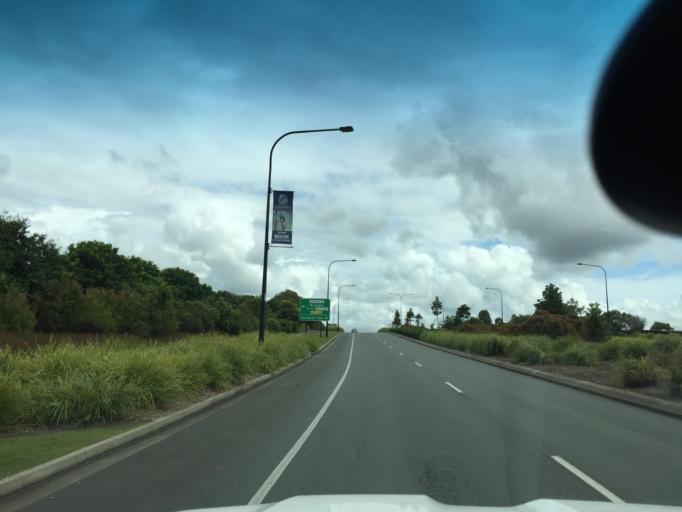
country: AU
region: Queensland
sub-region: Moreton Bay
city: Deception Bay
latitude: -27.2117
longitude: 152.9989
